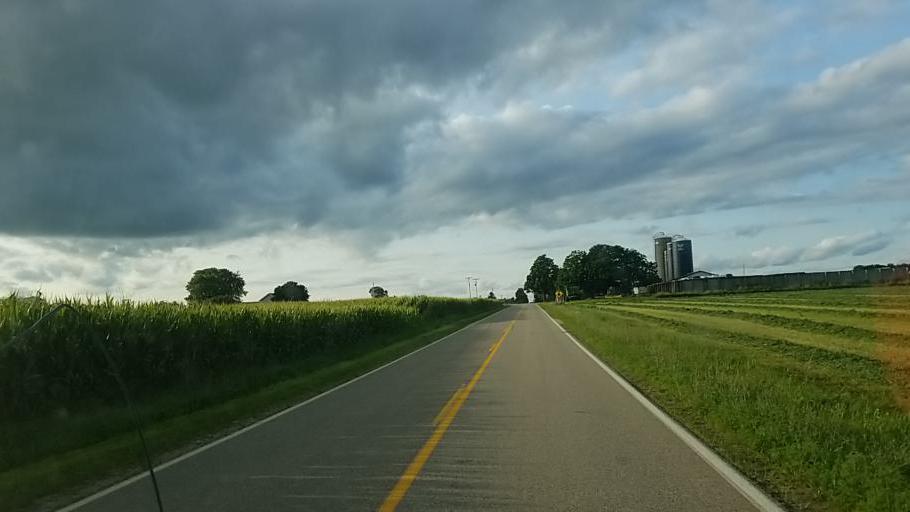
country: US
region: Michigan
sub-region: Montcalm County
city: Howard City
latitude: 43.3205
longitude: -85.3828
